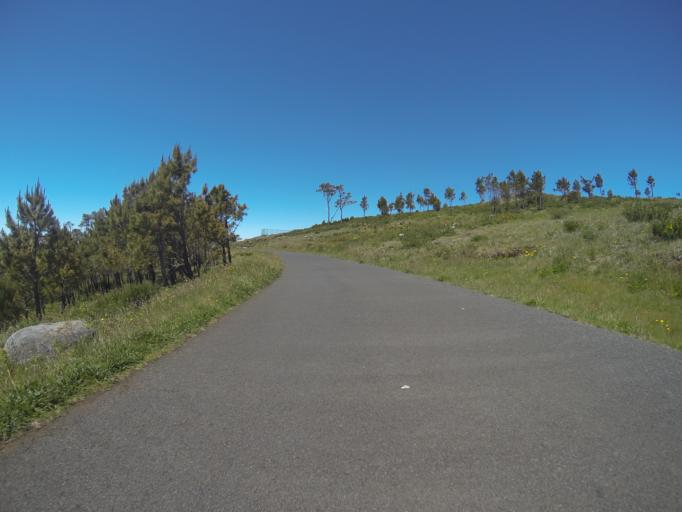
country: PT
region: Madeira
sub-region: Funchal
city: Nossa Senhora do Monte
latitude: 32.7185
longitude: -16.9127
